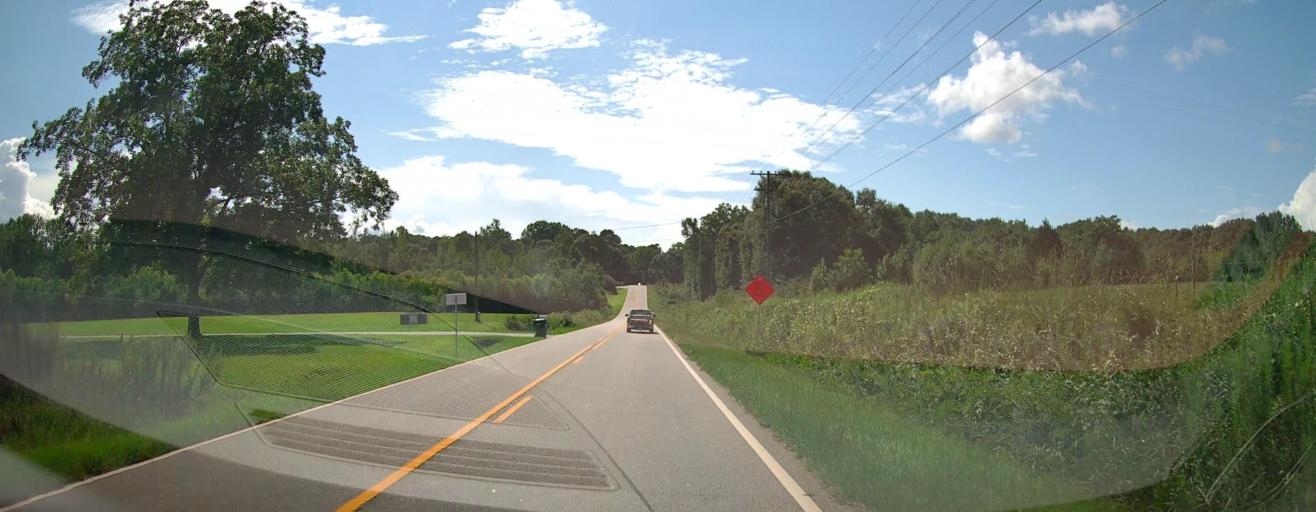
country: US
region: Georgia
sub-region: Upson County
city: Hannahs Mill
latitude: 32.9506
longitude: -84.2928
